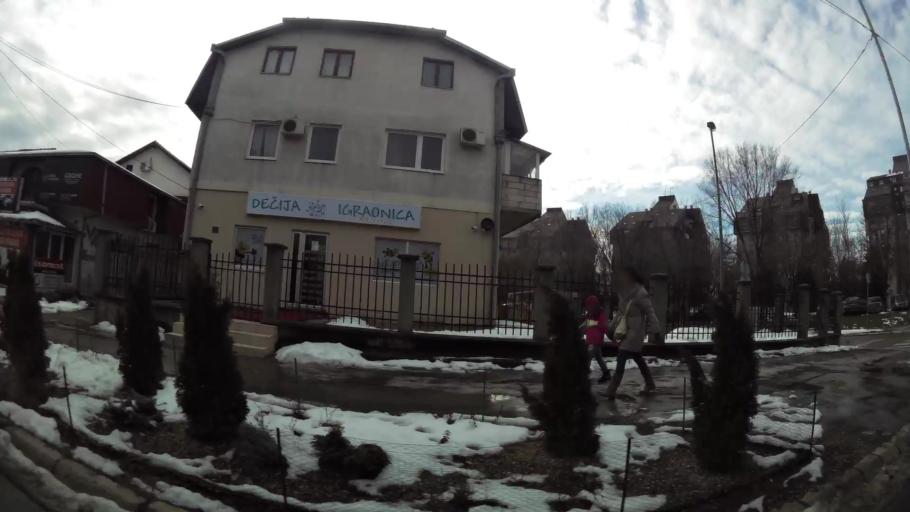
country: RS
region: Central Serbia
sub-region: Belgrade
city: Rakovica
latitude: 44.7376
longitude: 20.4214
